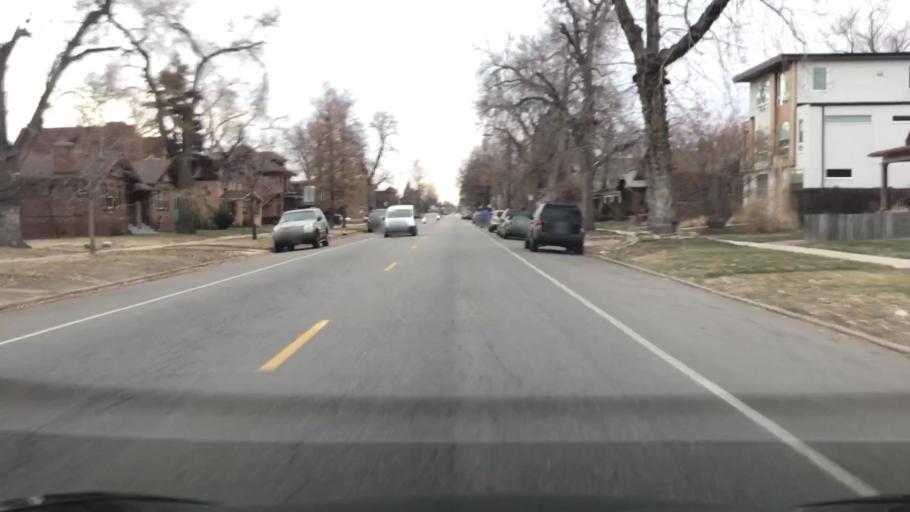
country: US
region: Colorado
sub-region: Denver County
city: Denver
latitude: 39.7016
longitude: -104.9828
